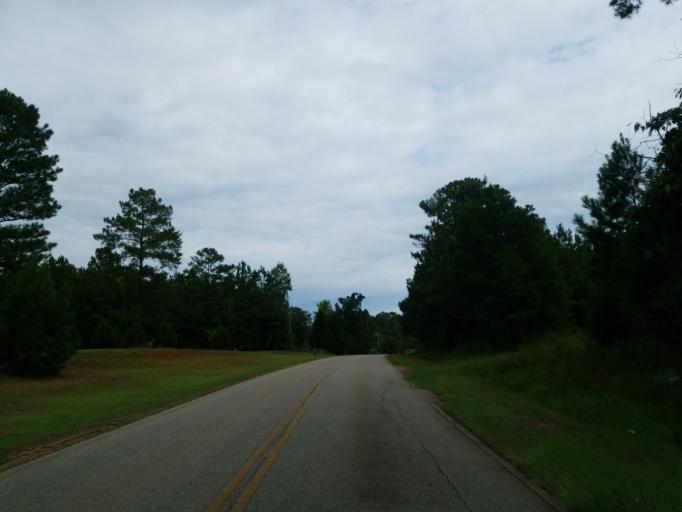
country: US
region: Georgia
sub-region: Bibb County
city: West Point
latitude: 32.9045
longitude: -83.8497
